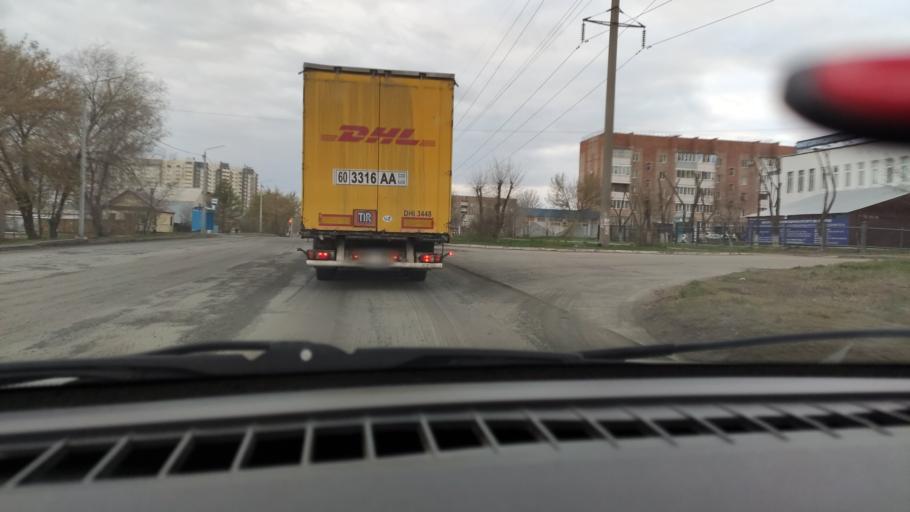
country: RU
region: Orenburg
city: Orenburg
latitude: 51.7858
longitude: 55.1782
